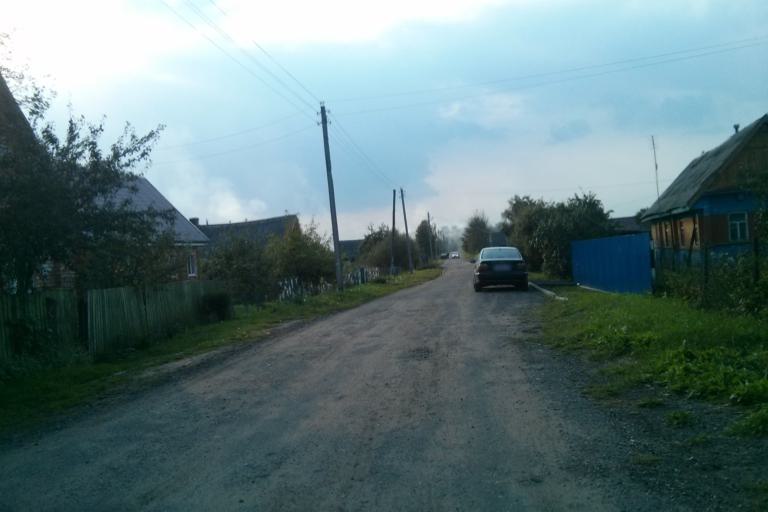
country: BY
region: Minsk
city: Chervyen'
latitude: 53.7152
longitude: 28.4118
